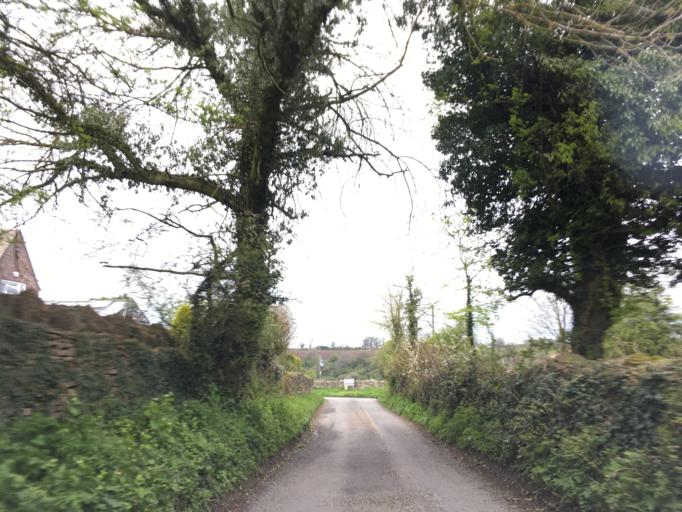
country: GB
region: England
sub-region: Gloucestershire
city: Stonehouse
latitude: 51.6988
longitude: -2.2844
